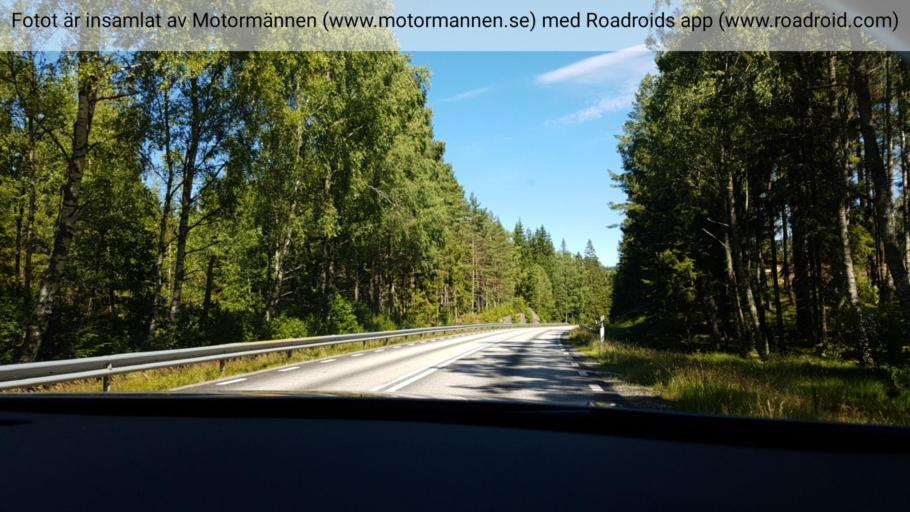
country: SE
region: Joenkoeping
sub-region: Gnosjo Kommun
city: Hillerstorp
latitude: 57.3303
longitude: 13.8119
